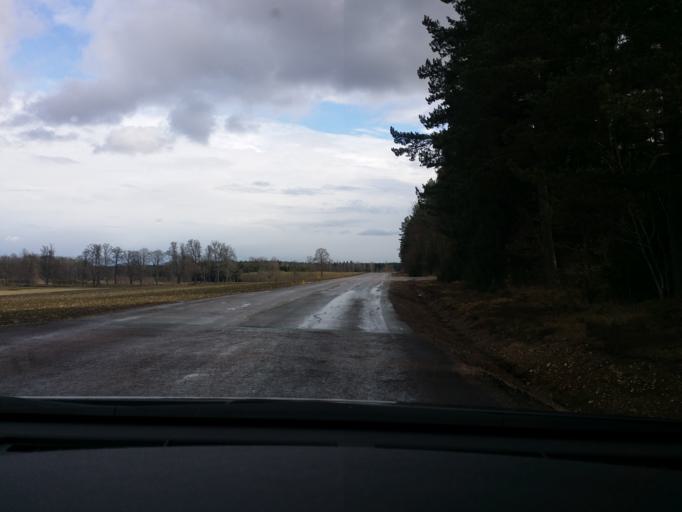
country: SE
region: Soedermanland
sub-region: Eskilstuna Kommun
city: Arla
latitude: 59.3100
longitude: 16.6822
